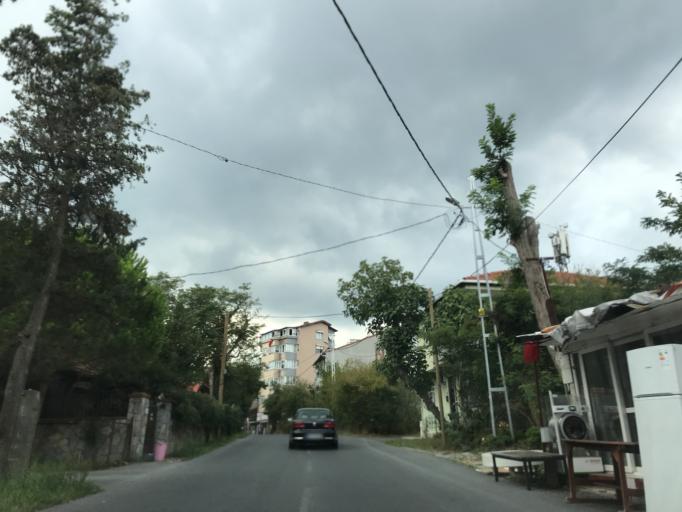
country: TR
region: Istanbul
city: Arikoey
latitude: 41.1778
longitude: 29.0521
